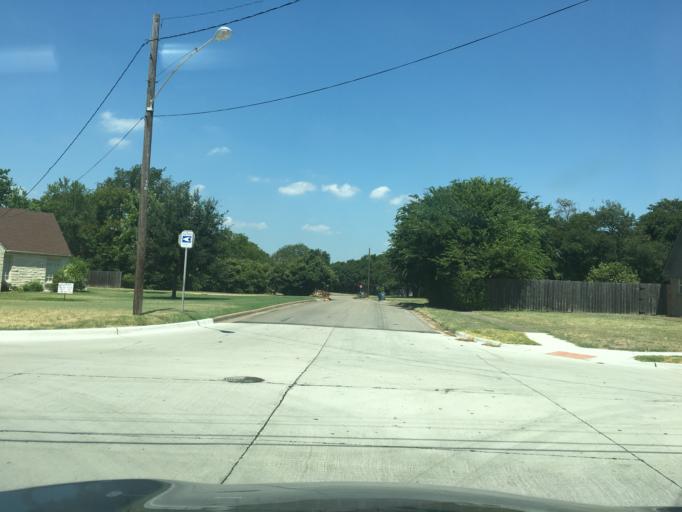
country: US
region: Texas
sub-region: Dallas County
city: Garland
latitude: 32.8664
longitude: -96.6877
